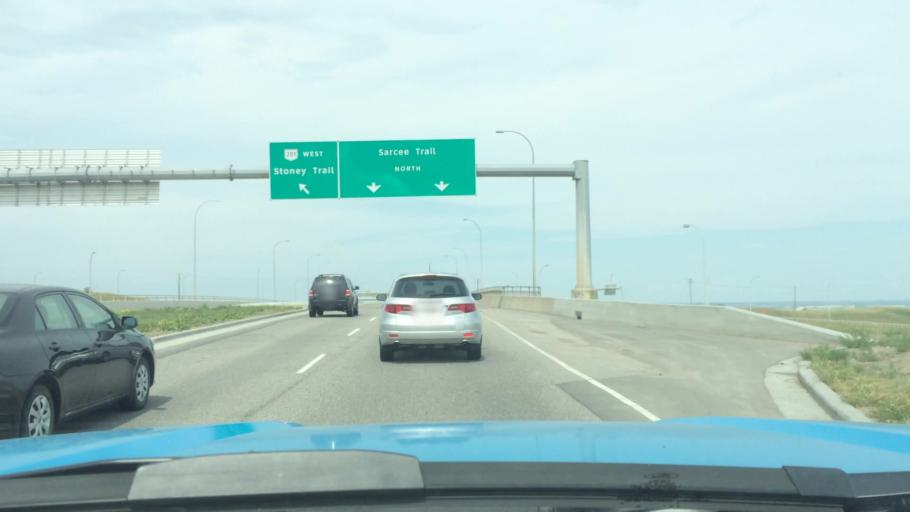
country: CA
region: Alberta
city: Calgary
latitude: 51.1509
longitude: -114.1662
